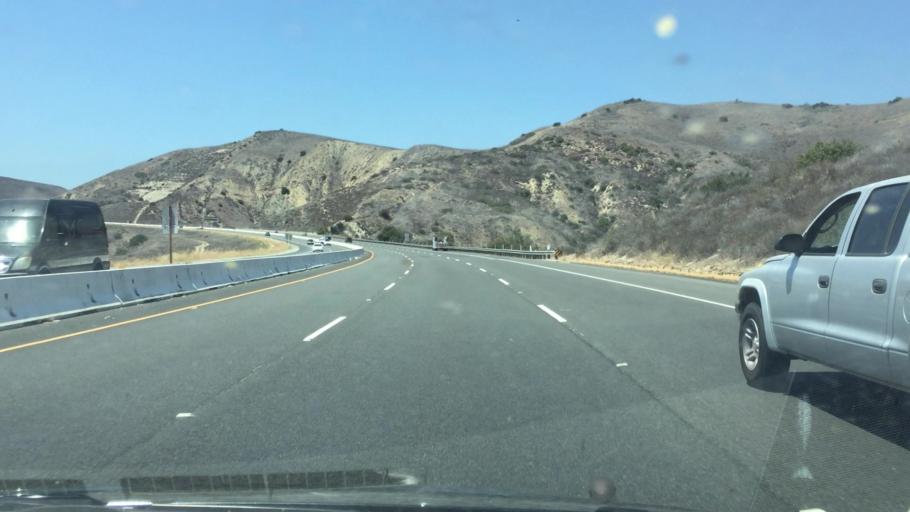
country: US
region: California
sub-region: Orange County
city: North Tustin
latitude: 33.7427
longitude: -117.7185
